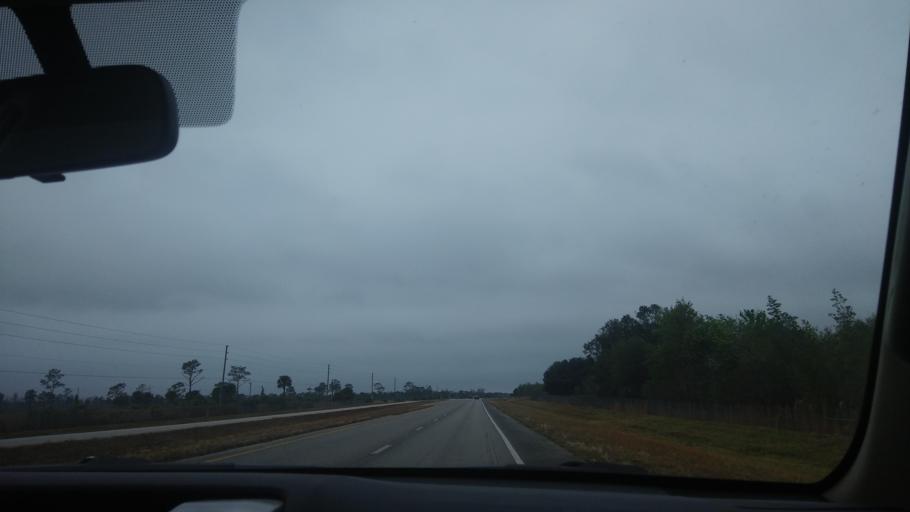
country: US
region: Florida
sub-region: Osceola County
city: Saint Cloud
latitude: 28.1313
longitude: -81.0073
